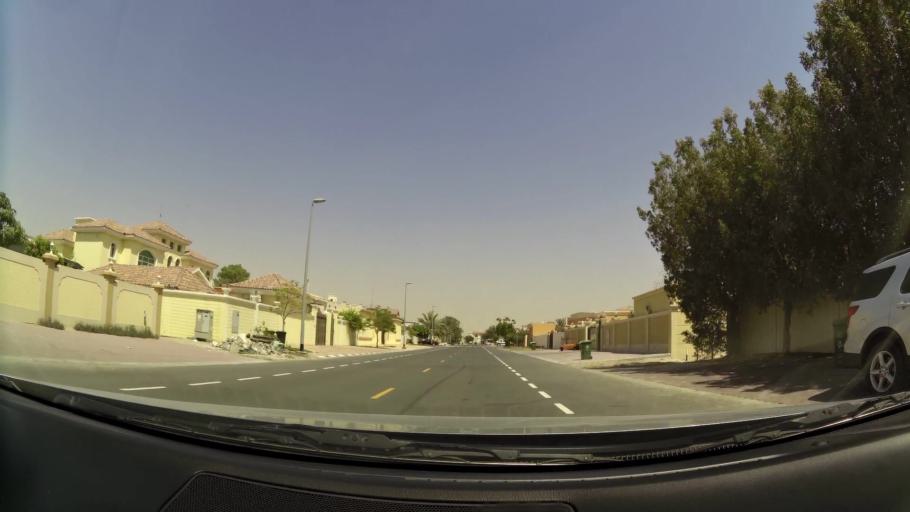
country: AE
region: Dubai
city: Dubai
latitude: 25.1046
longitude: 55.2106
